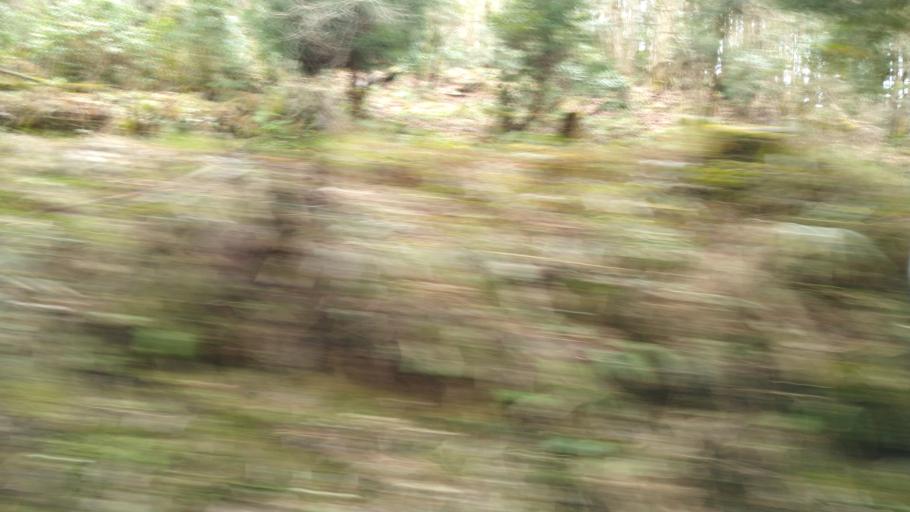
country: JP
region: Kyoto
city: Ayabe
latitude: 35.3166
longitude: 135.3655
